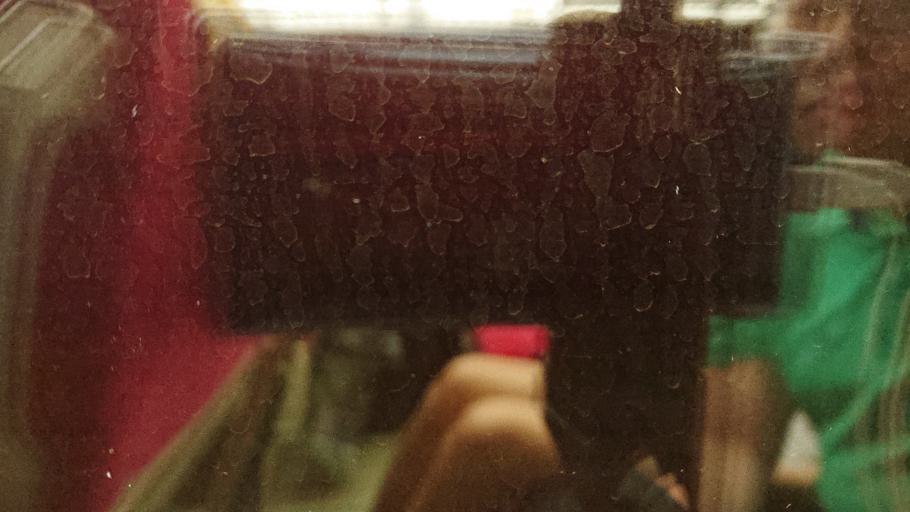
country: TW
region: Taiwan
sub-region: Keelung
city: Keelung
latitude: 25.0292
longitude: 121.8690
